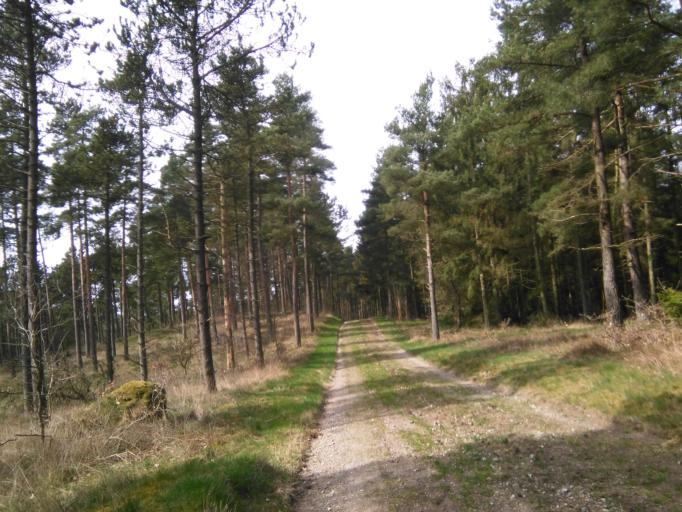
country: DK
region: Central Jutland
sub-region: Odder Kommune
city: Odder
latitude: 55.8883
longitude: 10.0904
